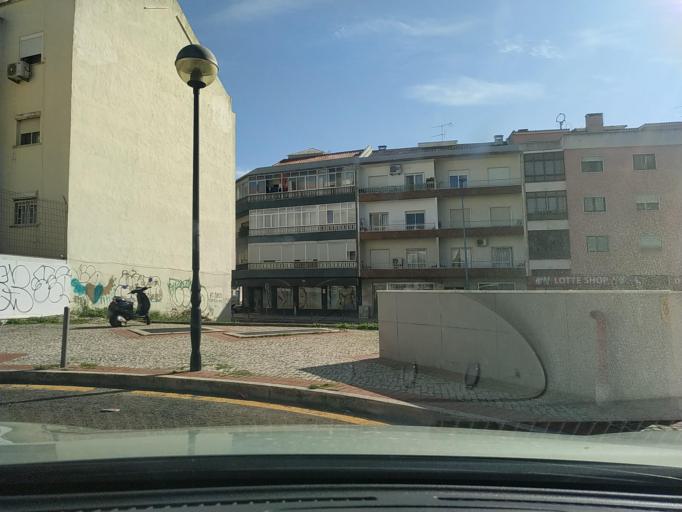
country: PT
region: Lisbon
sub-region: Amadora
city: Amadora
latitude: 38.7608
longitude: -9.2418
